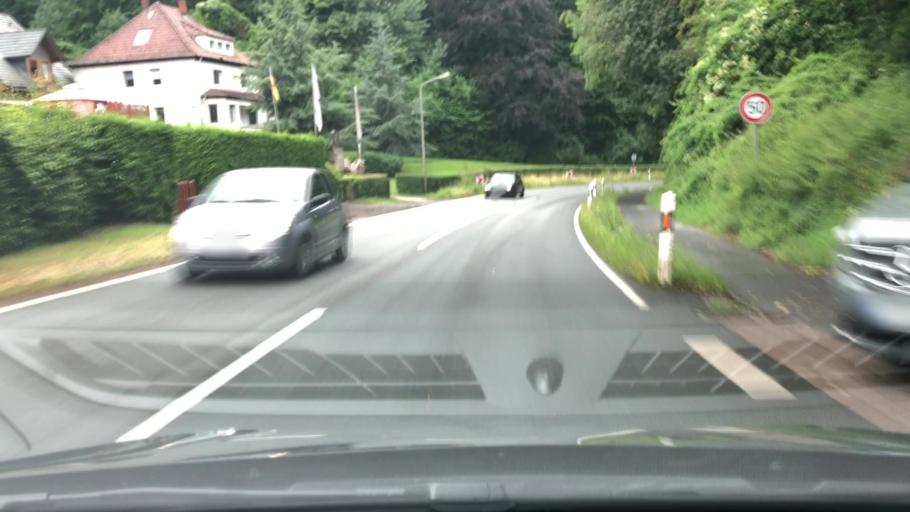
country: DE
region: North Rhine-Westphalia
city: Porta Westfalica
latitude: 52.2387
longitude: 8.9334
